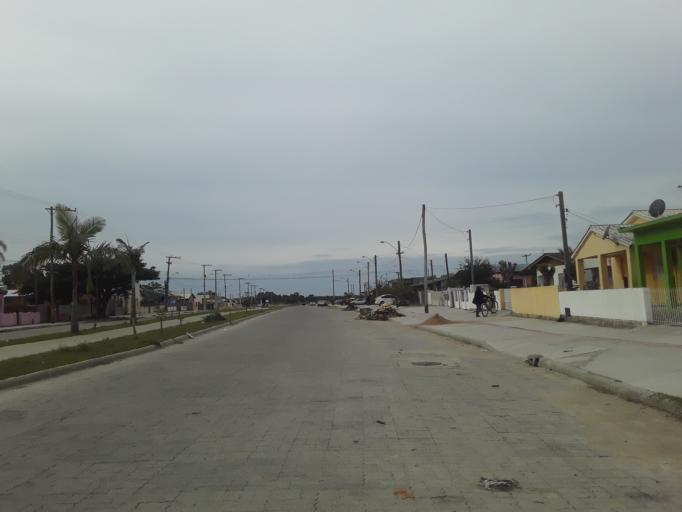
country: BR
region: Rio Grande do Sul
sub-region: Sao Lourenco Do Sul
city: Sao Lourenco do Sul
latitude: -31.3444
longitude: -51.9902
